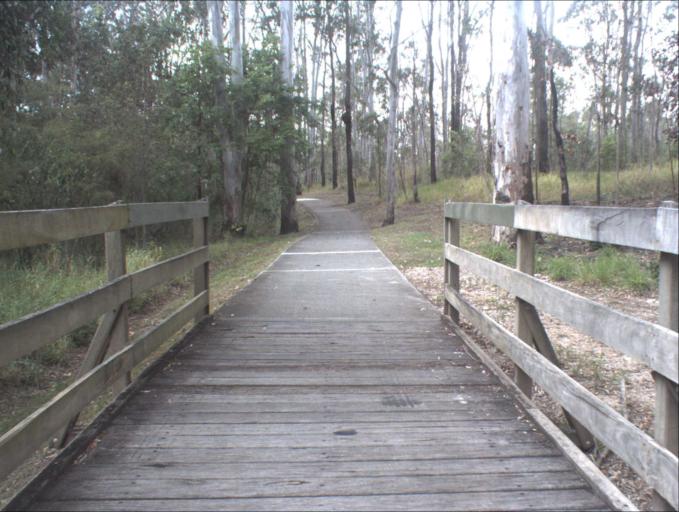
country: AU
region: Queensland
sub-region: Logan
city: Slacks Creek
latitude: -27.6453
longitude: 153.1396
